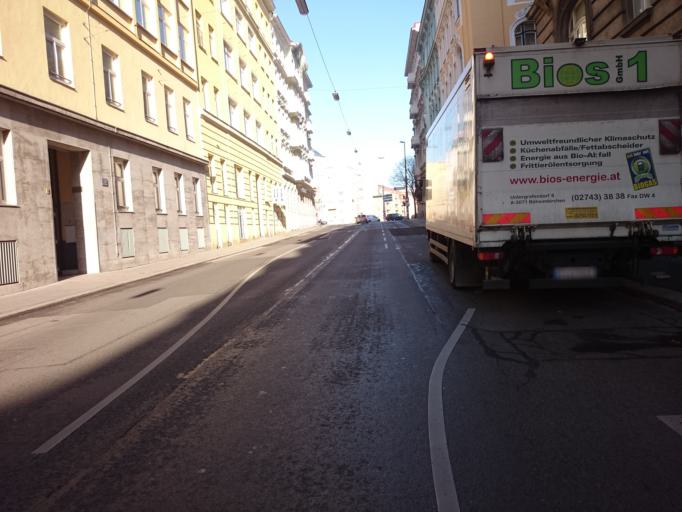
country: AT
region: Vienna
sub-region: Wien Stadt
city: Vienna
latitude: 48.2318
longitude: 16.3561
